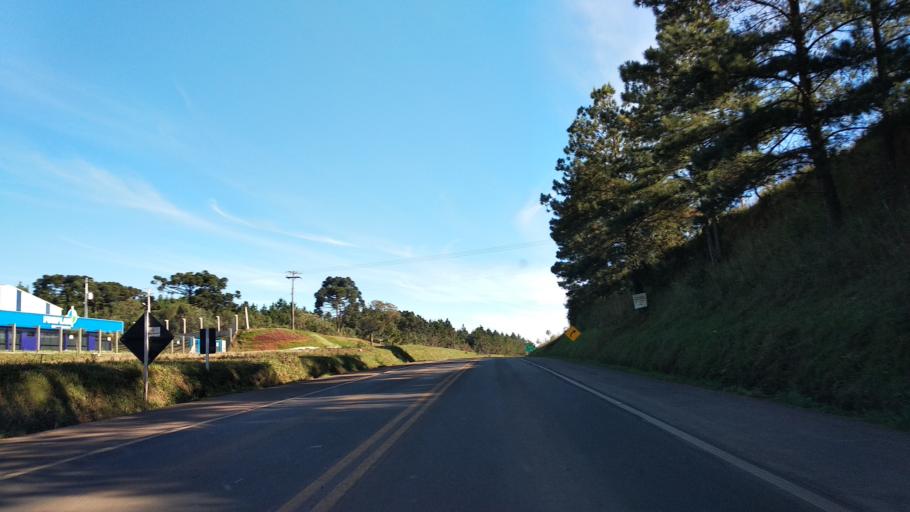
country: BR
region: Santa Catarina
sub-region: Campos Novos
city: Campos Novos
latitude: -27.4061
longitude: -51.2076
